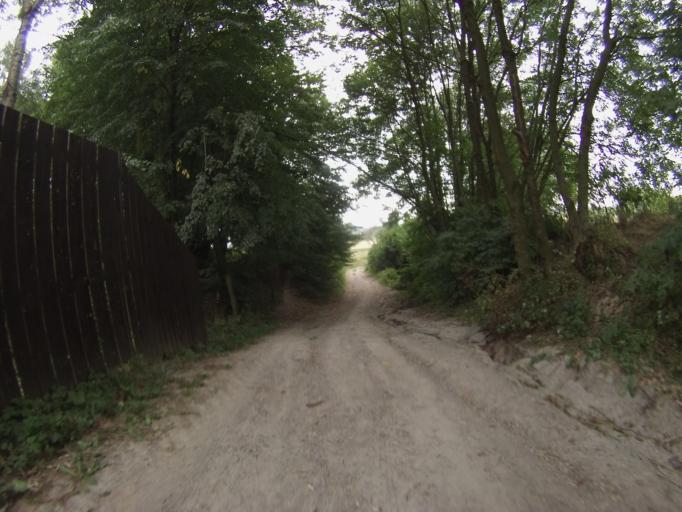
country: PL
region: Swietokrzyskie
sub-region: Powiat staszowski
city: Bogoria
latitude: 50.6865
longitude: 21.2453
